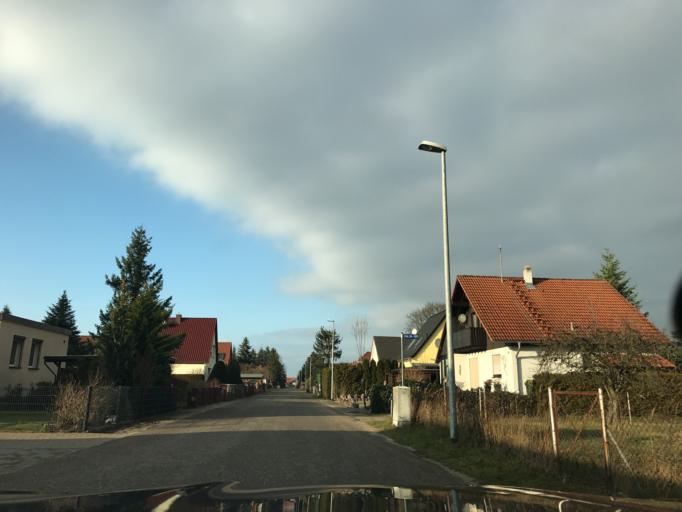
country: DE
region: Brandenburg
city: Brandenburg an der Havel
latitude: 52.3728
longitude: 12.5325
